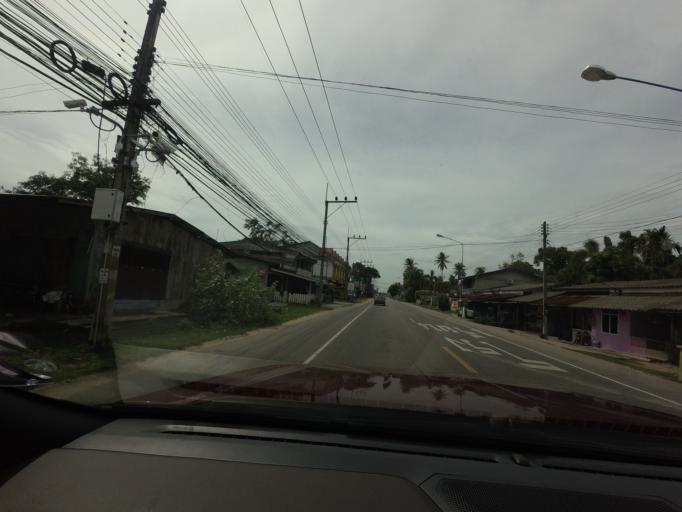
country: TH
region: Narathiwat
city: Tak Bai
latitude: 6.2405
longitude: 102.0796
